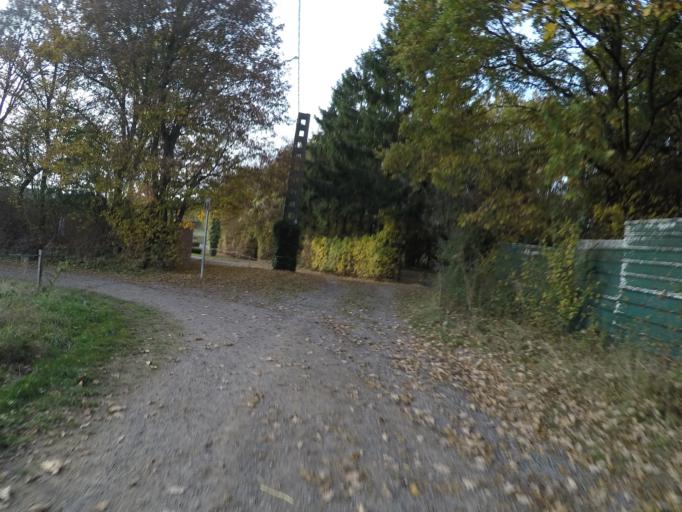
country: BE
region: Wallonia
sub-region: Province du Luxembourg
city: Hotton
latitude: 50.2871
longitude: 5.4956
